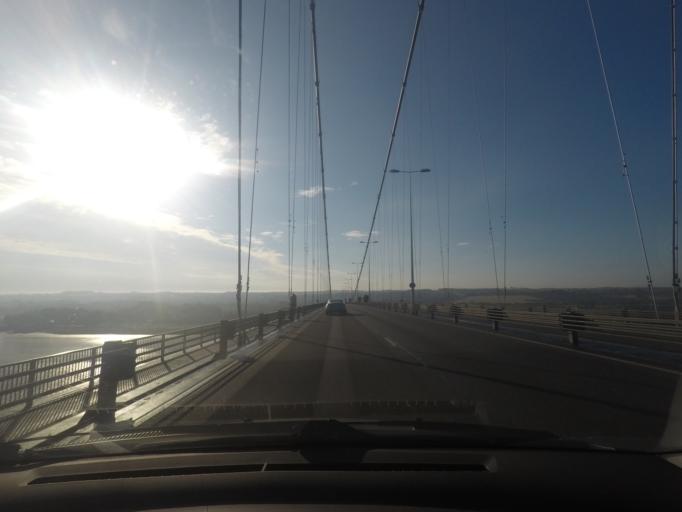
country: GB
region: England
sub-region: North Lincolnshire
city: Barton upon Humber
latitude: 53.7004
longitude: -0.4496
